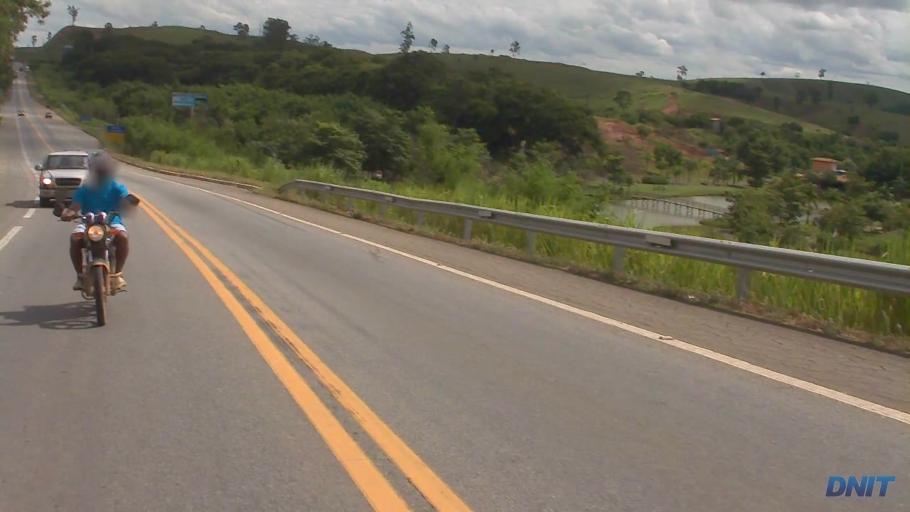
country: BR
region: Minas Gerais
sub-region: Ipatinga
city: Ipatinga
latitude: -19.4387
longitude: -42.5109
